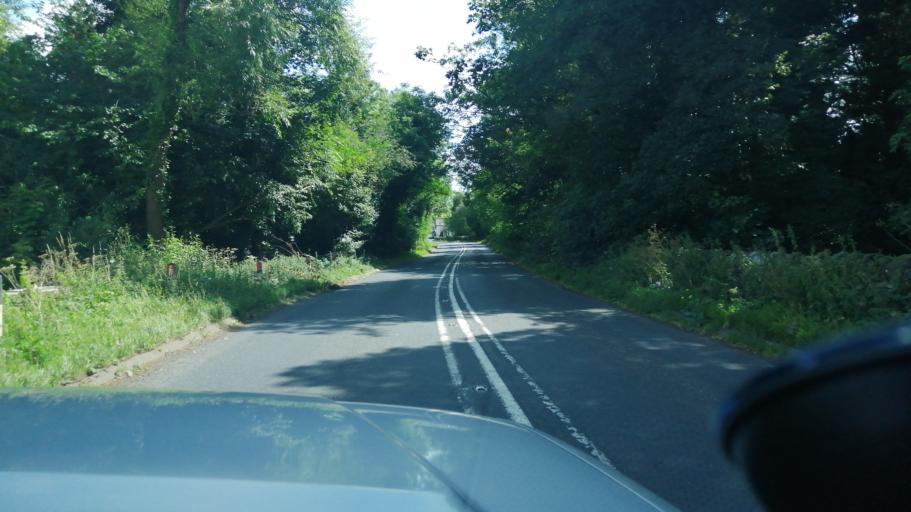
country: GB
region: England
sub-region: Herefordshire
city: Kinnersley
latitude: 52.1128
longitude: -2.9690
